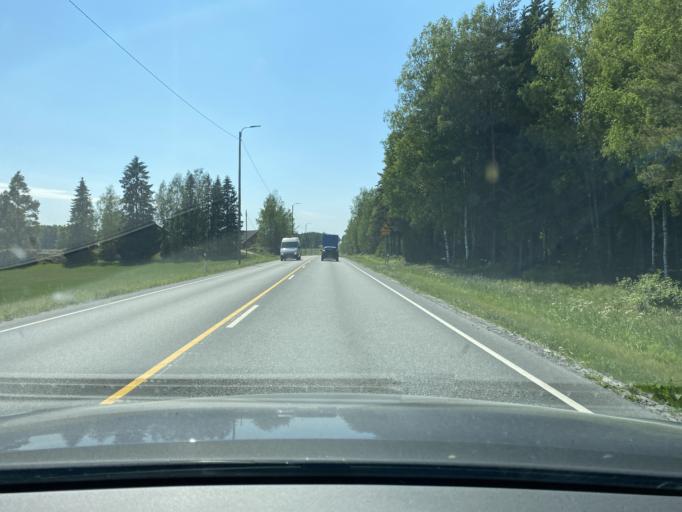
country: FI
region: Pirkanmaa
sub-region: Lounais-Pirkanmaa
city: Mouhijaervi
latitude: 61.3547
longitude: 23.0778
